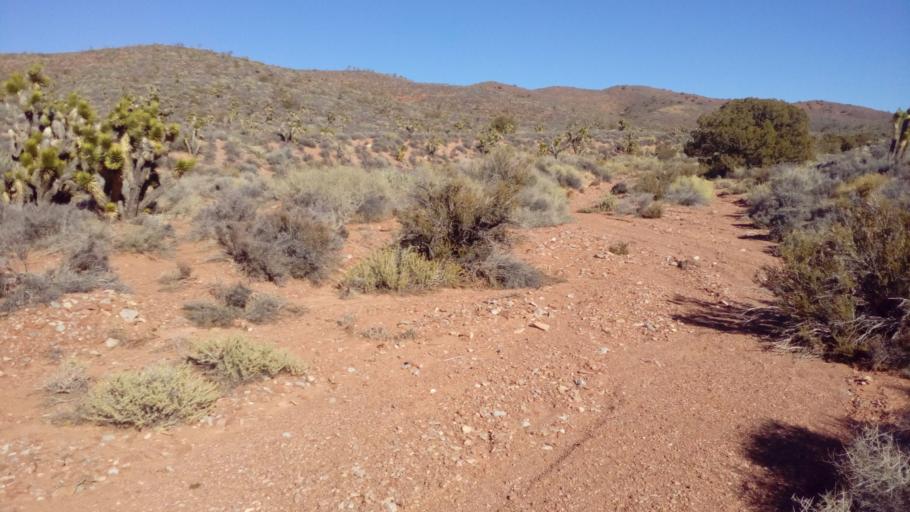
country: US
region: Nevada
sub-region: Clark County
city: Sandy Valley
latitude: 36.0617
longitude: -115.5862
